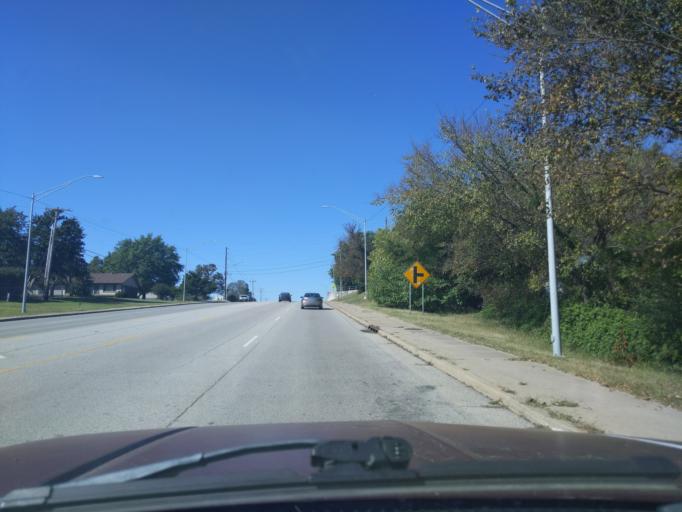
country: US
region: Oklahoma
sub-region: Creek County
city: Sapulpa
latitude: 35.9885
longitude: -96.0883
